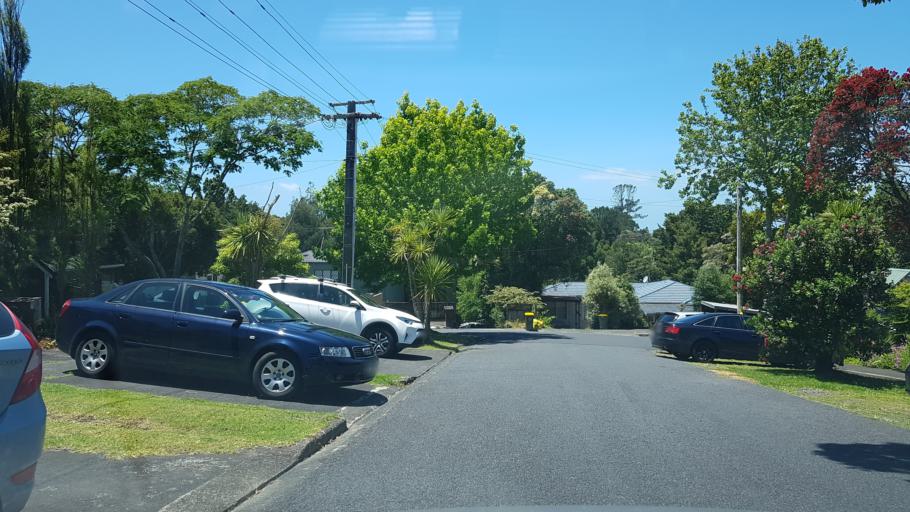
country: NZ
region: Auckland
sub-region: Auckland
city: North Shore
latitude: -36.8068
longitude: 174.7276
